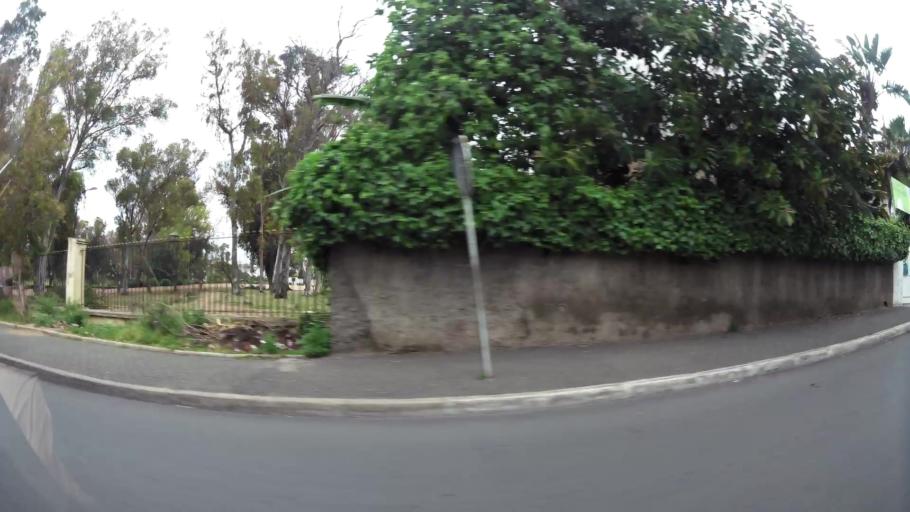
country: MA
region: Grand Casablanca
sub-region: Casablanca
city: Casablanca
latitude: 33.5628
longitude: -7.6145
